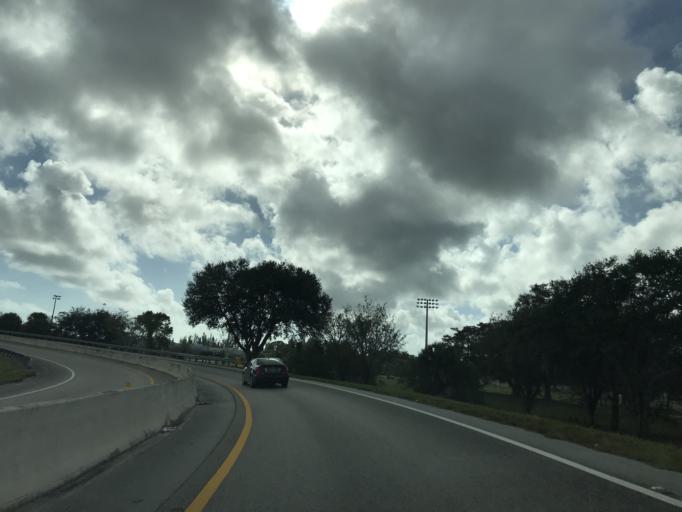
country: US
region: Florida
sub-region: Broward County
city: Coconut Creek
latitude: 26.2714
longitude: -80.1709
